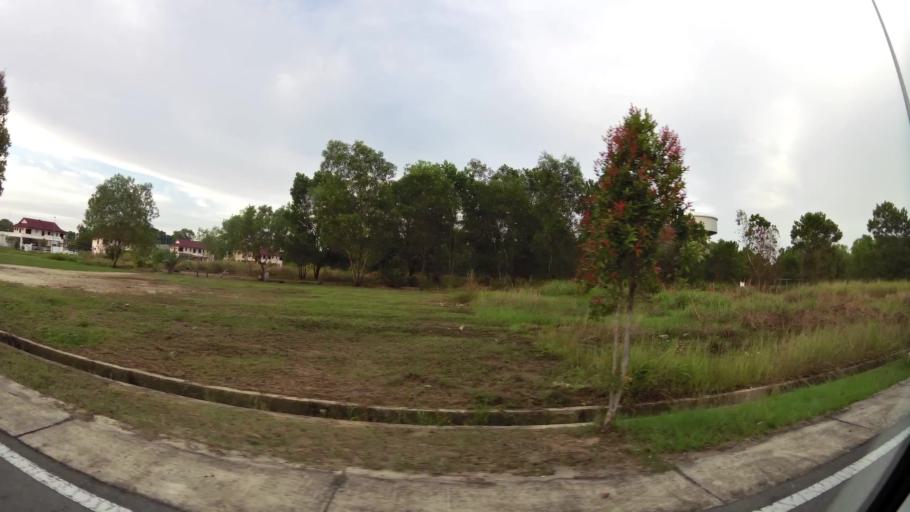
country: BN
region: Brunei and Muara
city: Bandar Seri Begawan
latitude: 4.9950
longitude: 114.9890
